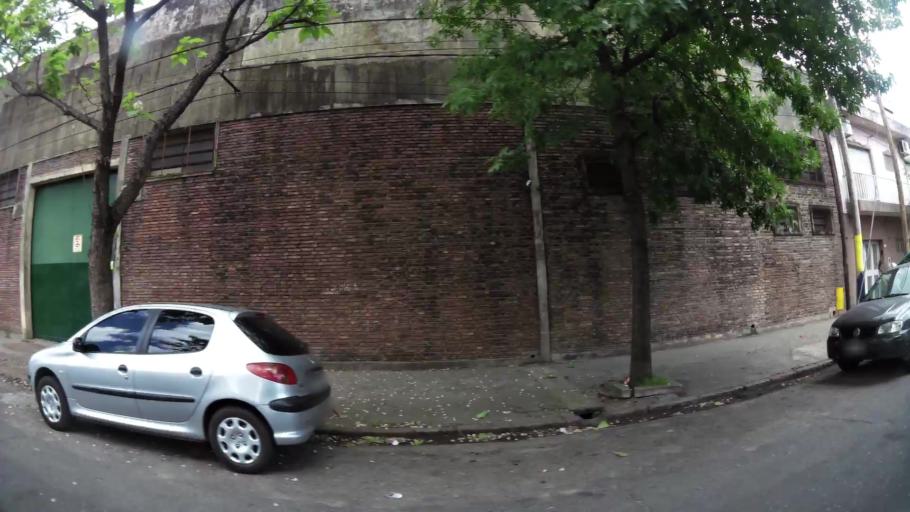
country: AR
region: Santa Fe
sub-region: Departamento de Rosario
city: Rosario
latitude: -32.9766
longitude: -60.6355
